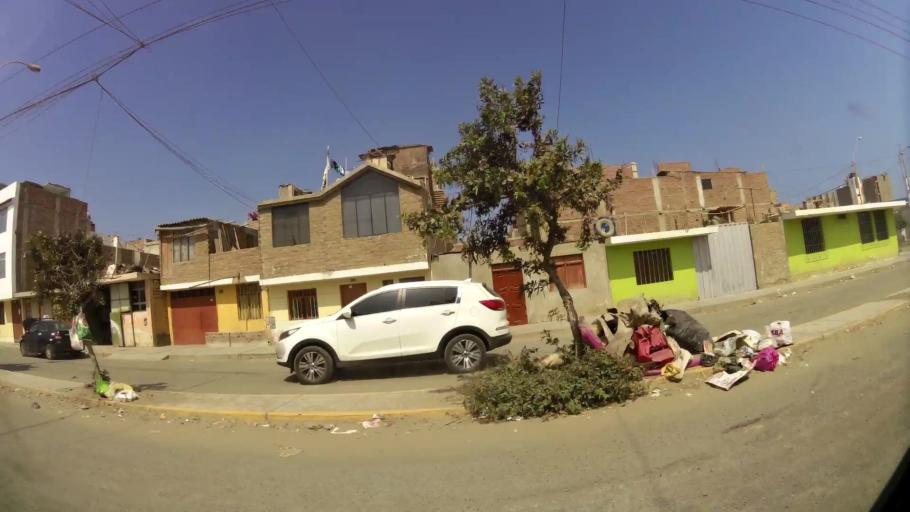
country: PE
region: La Libertad
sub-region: Provincia de Trujillo
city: Buenos Aires
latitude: -8.1314
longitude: -79.0509
